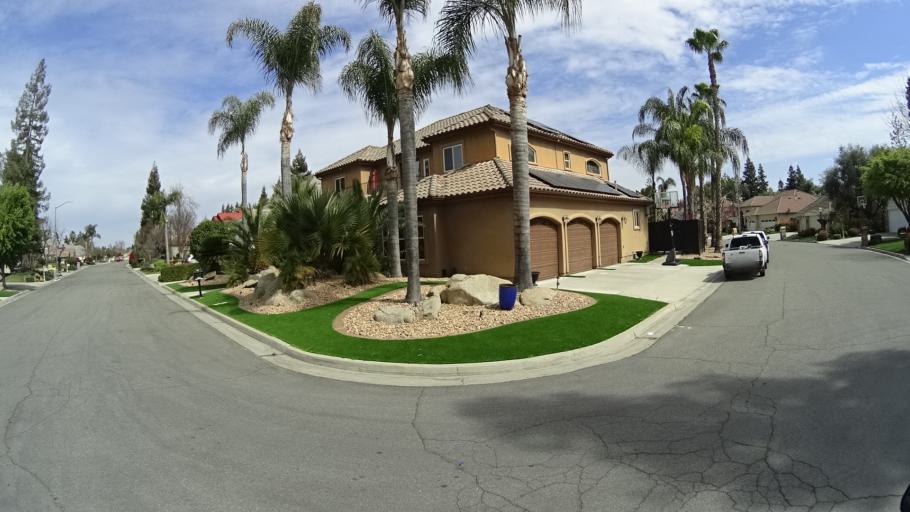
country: US
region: California
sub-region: Fresno County
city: West Park
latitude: 36.8423
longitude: -119.8833
